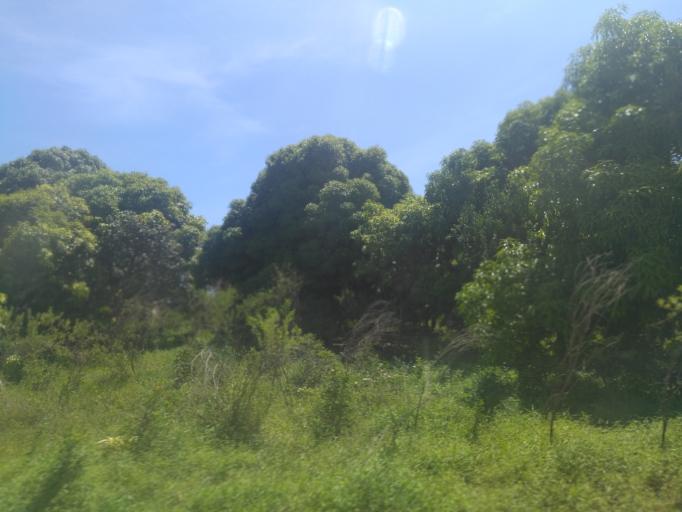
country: TZ
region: Zanzibar North
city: Gamba
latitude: -5.9291
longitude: 39.3421
